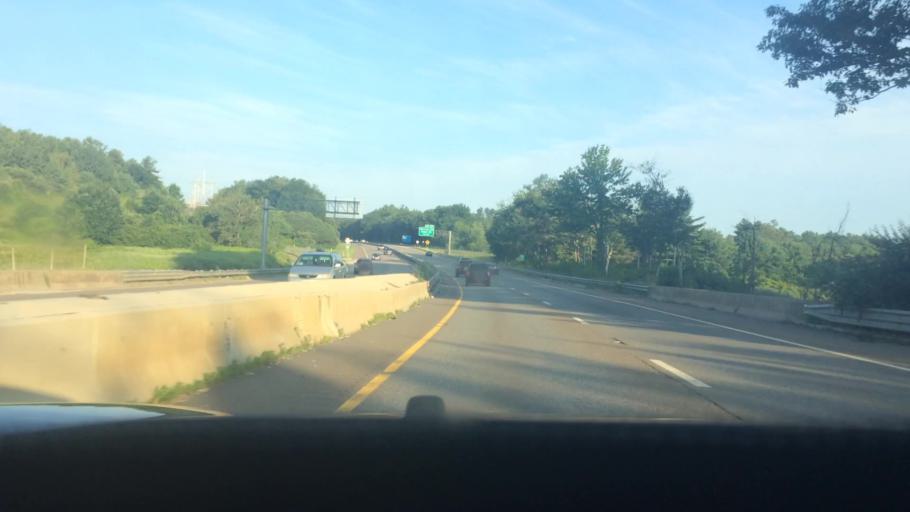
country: US
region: Massachusetts
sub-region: Worcester County
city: Fitchburg
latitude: 42.5498
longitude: -71.8475
